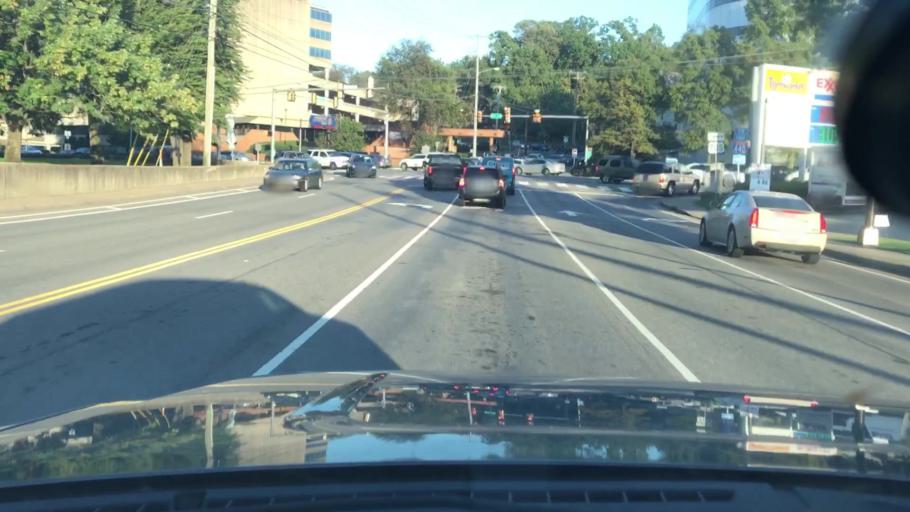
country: US
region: Tennessee
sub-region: Davidson County
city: Nashville
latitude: 36.1395
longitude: -86.8199
